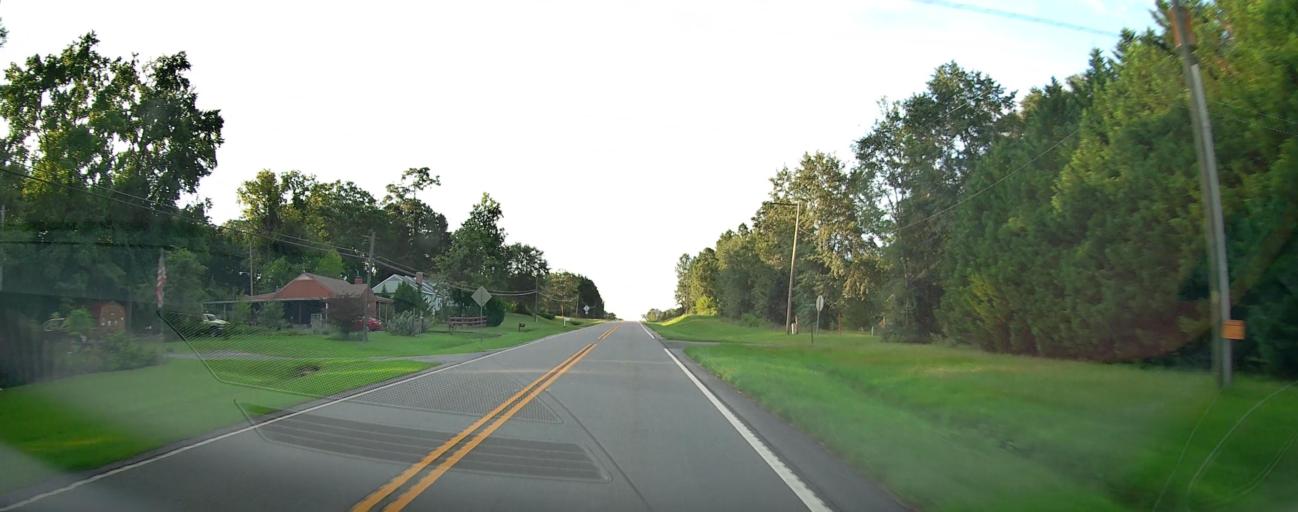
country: US
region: Georgia
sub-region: Taylor County
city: Reynolds
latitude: 32.5773
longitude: -84.0898
